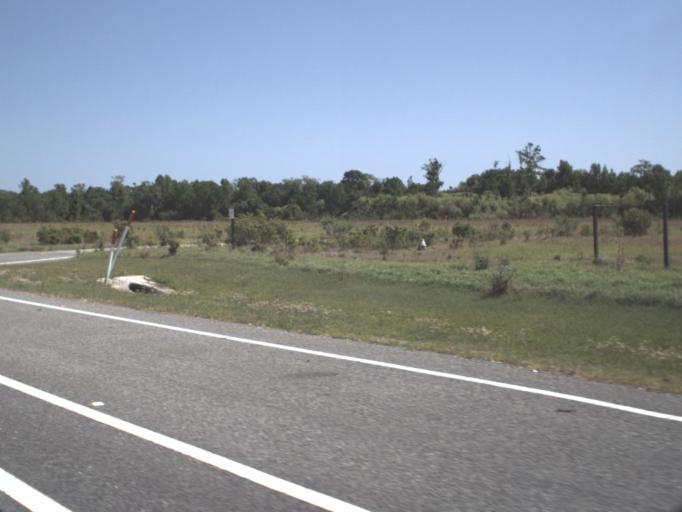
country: US
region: Florida
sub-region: Flagler County
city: Palm Coast
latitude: 29.6049
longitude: -81.2821
